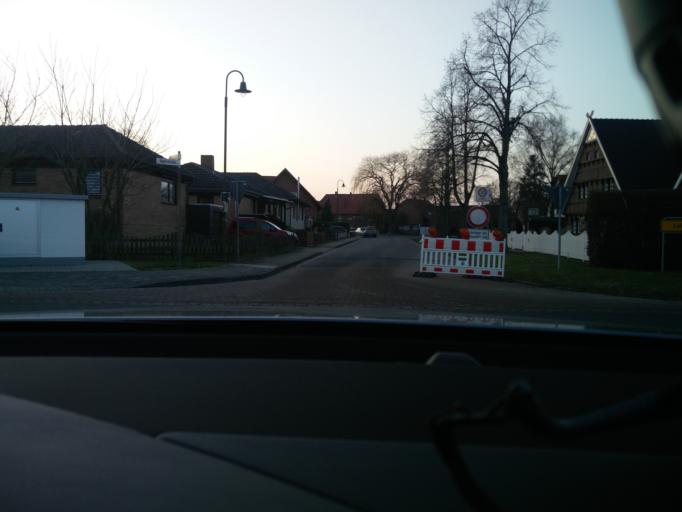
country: DE
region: Lower Saxony
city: Sehnde
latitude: 52.3183
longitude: 10.0256
